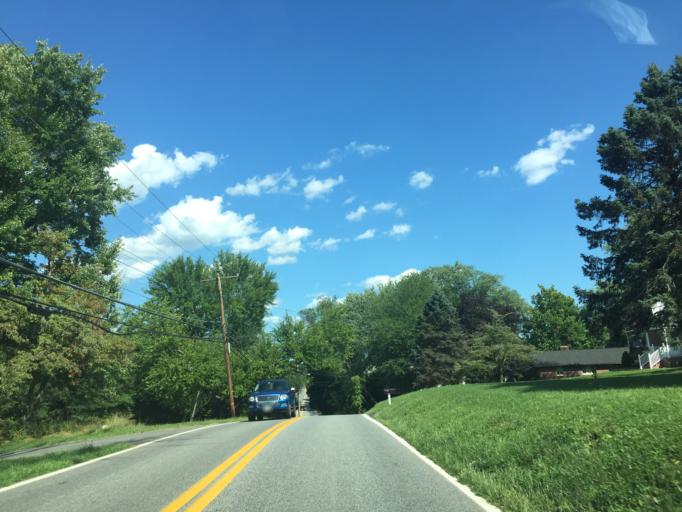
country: US
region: Maryland
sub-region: Baltimore County
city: Perry Hall
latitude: 39.4146
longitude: -76.4372
